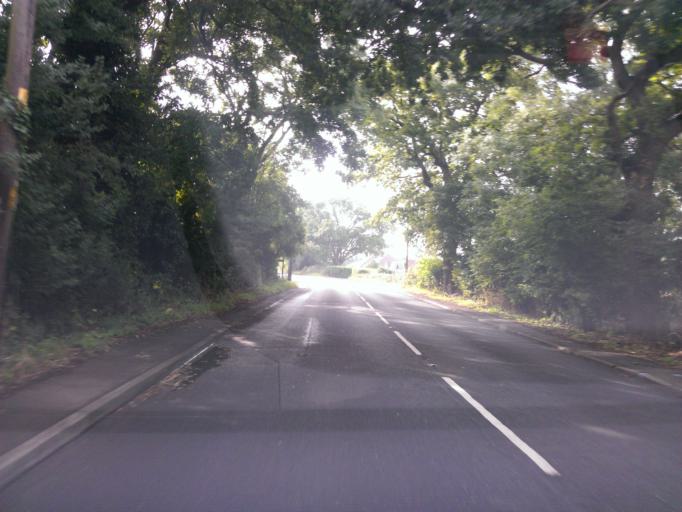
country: GB
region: England
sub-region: Essex
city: Little Clacton
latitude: 51.8383
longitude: 1.1320
